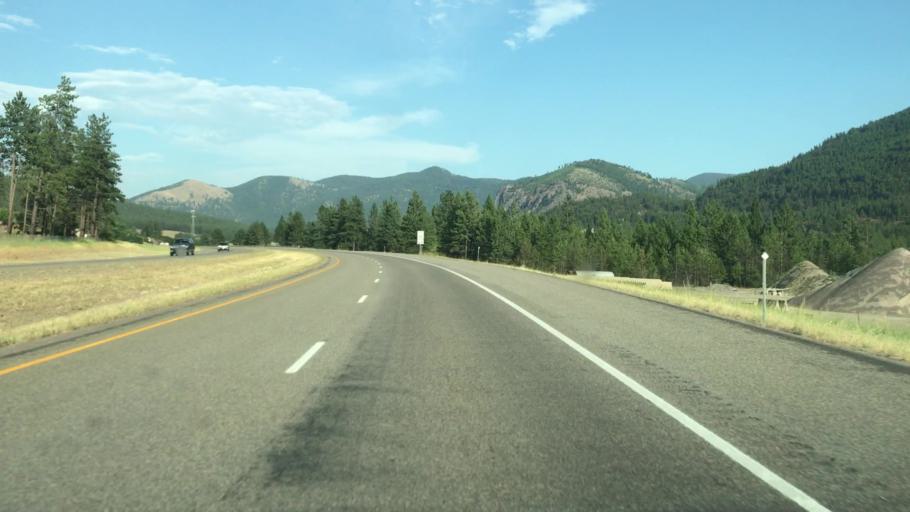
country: US
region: Montana
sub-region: Missoula County
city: Frenchtown
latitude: 47.0012
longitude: -114.4849
